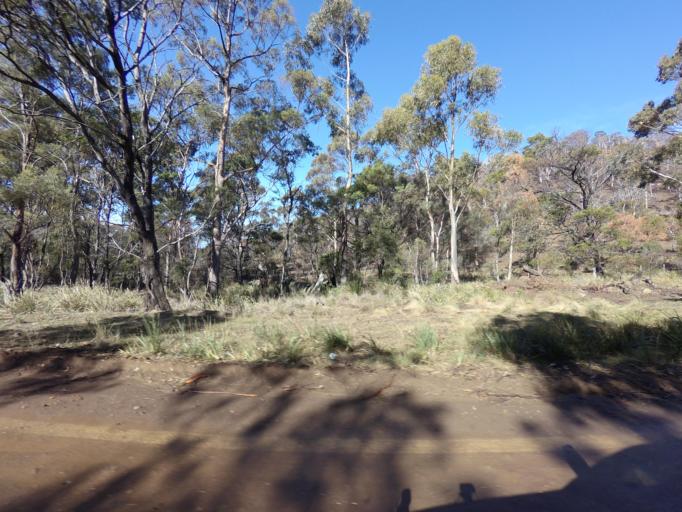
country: AU
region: Tasmania
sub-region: Sorell
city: Sorell
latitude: -42.4134
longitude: 147.9502
